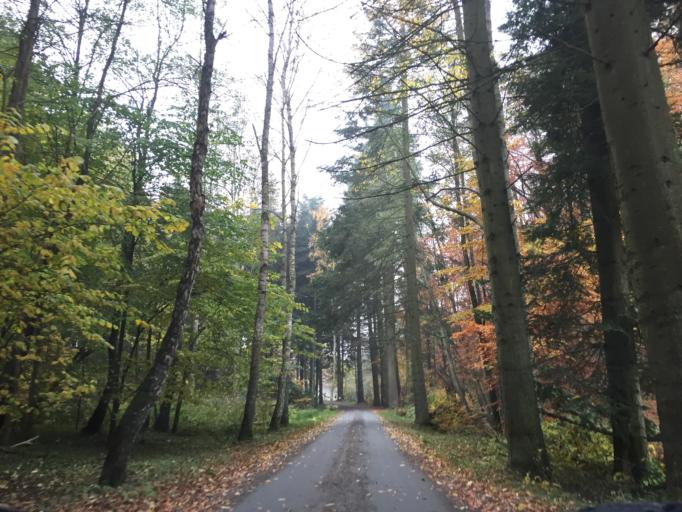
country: SE
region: Skane
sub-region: Lunds Kommun
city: Veberod
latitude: 55.6112
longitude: 13.5122
